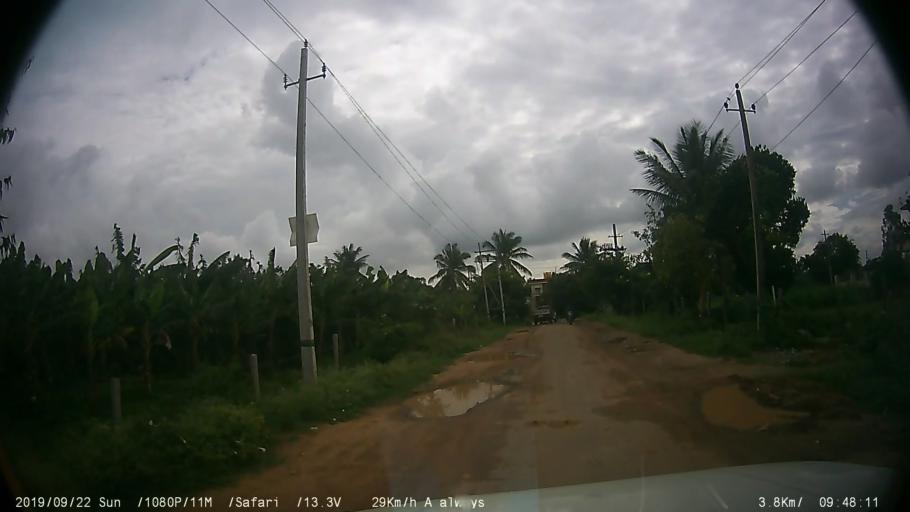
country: IN
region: Karnataka
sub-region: Bangalore Urban
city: Anekal
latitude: 12.8142
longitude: 77.6500
